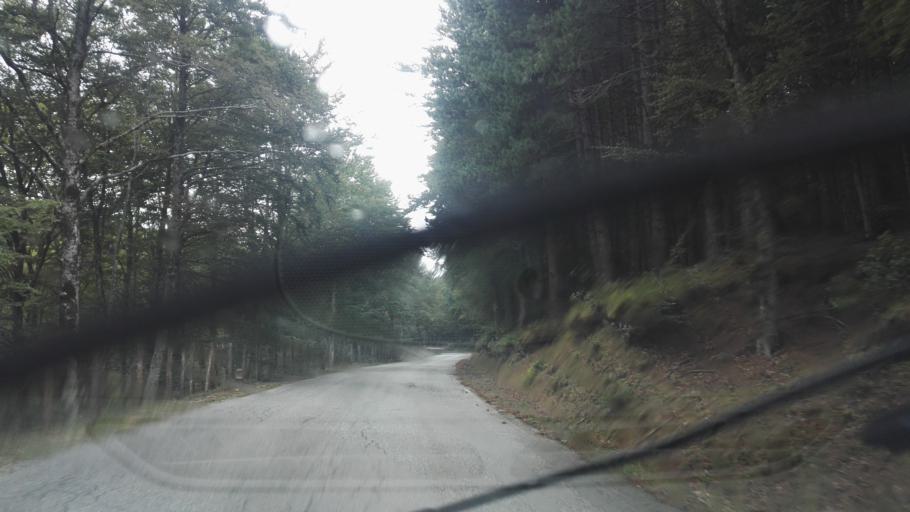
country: IT
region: Calabria
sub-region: Provincia di Vibo-Valentia
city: Nardodipace
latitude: 38.4886
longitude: 16.3744
